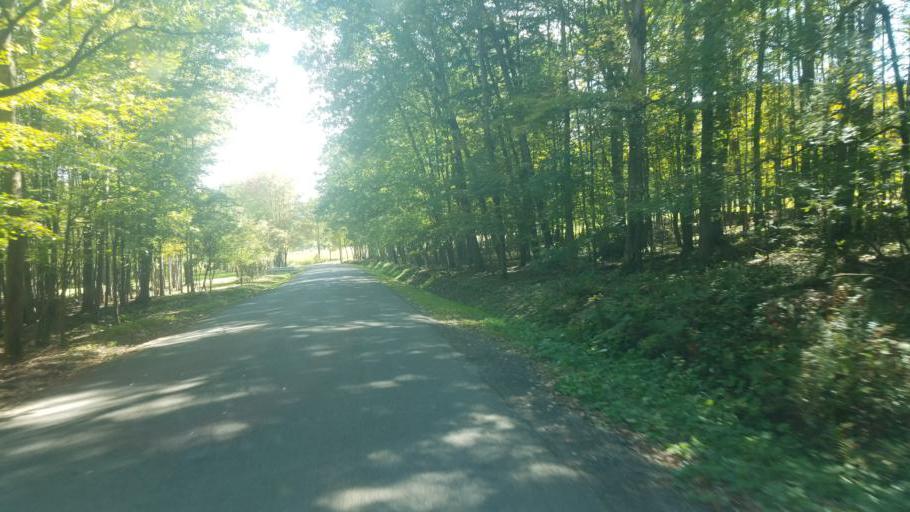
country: US
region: New York
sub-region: Allegany County
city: Cuba
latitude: 42.1712
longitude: -78.3528
